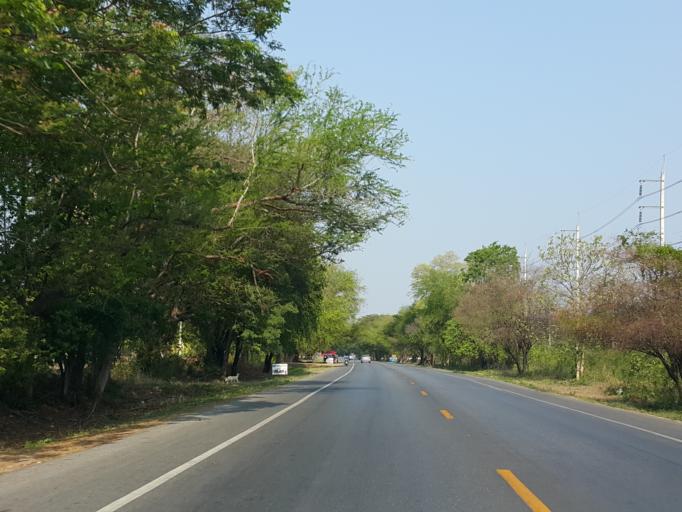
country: TH
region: Kanchanaburi
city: Sai Yok
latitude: 14.0899
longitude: 99.3137
